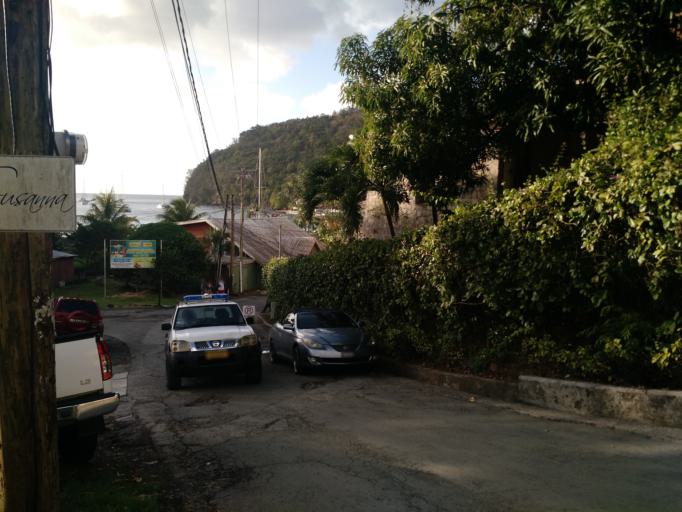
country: LC
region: Anse-la-Raye
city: Anse La Raye
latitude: 13.9644
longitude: -61.0241
